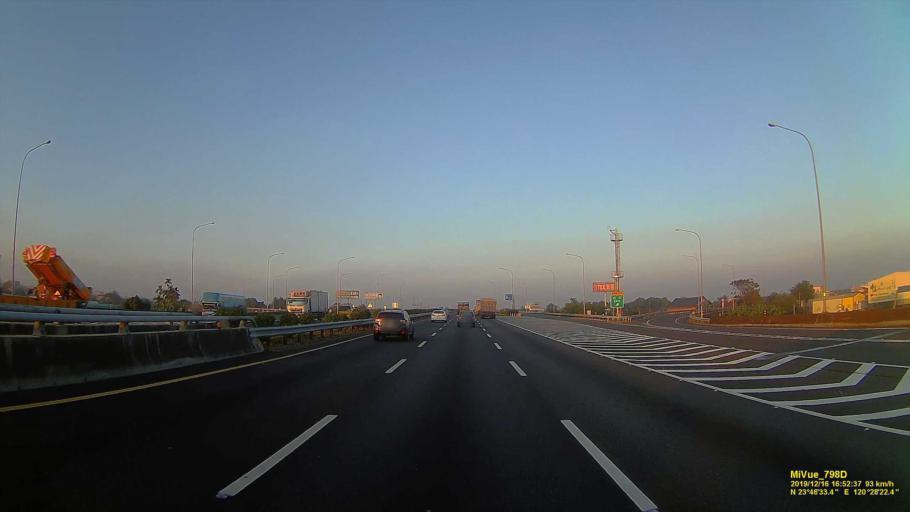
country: TW
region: Taiwan
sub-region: Yunlin
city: Douliu
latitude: 23.7754
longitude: 120.4731
